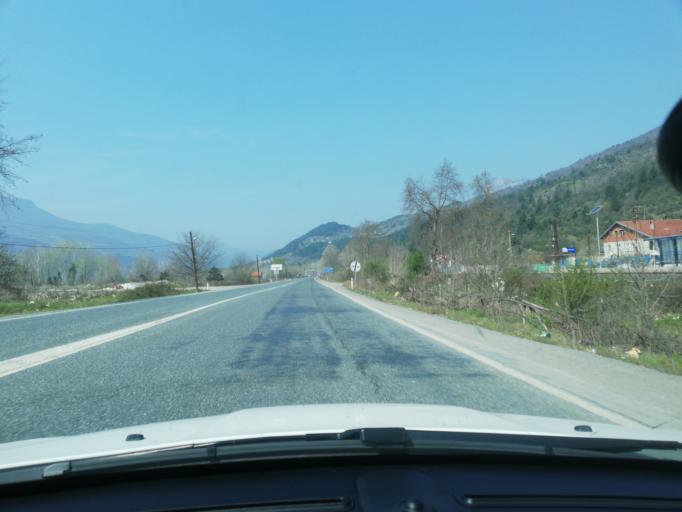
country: TR
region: Karabuk
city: Yenice
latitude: 41.2169
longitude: 32.3022
